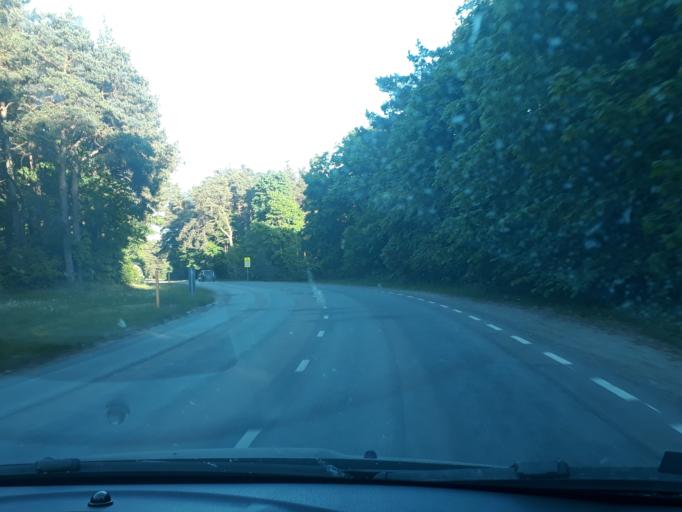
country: EE
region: Paernumaa
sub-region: Paernu linn
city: Parnu
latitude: 58.3863
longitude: 24.5328
